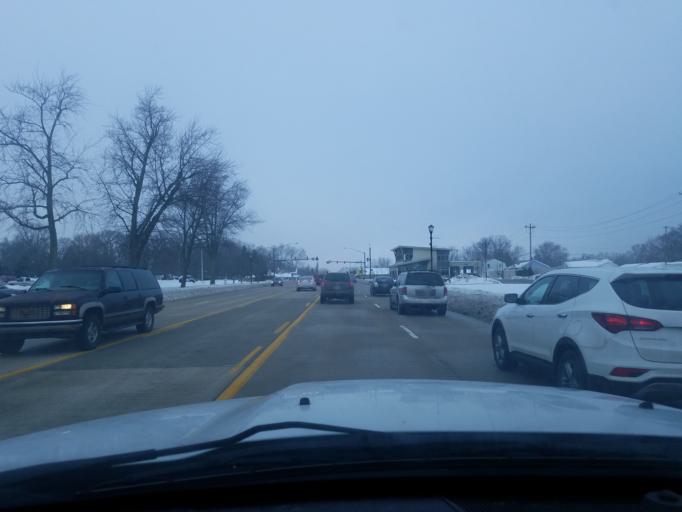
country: US
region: Indiana
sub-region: Saint Joseph County
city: Mishawaka
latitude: 41.6757
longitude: -86.1813
